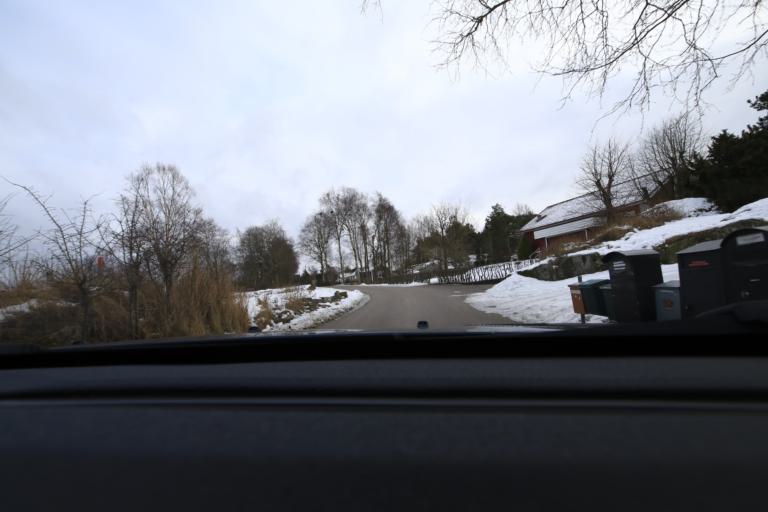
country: SE
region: Halland
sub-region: Kungsbacka Kommun
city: Frillesas
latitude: 57.2243
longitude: 12.1562
